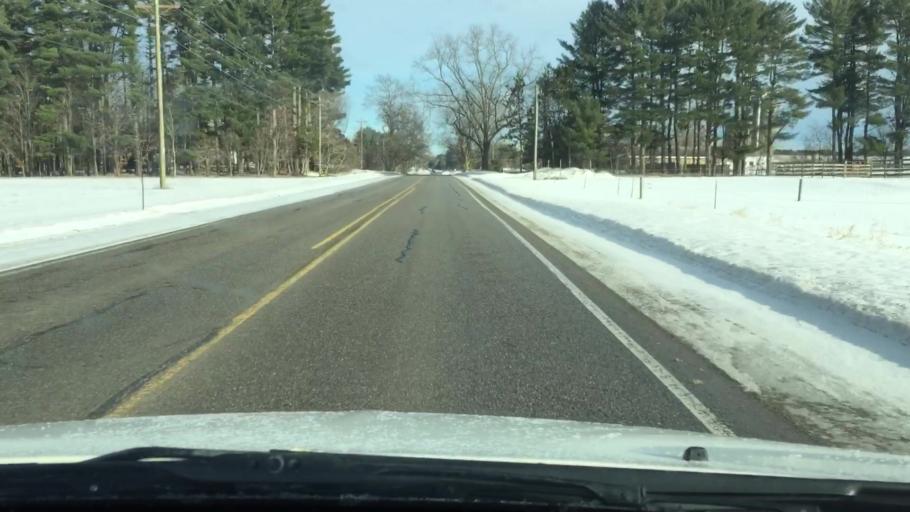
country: US
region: Michigan
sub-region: Kalkaska County
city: Kalkaska
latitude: 44.6410
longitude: -85.2596
